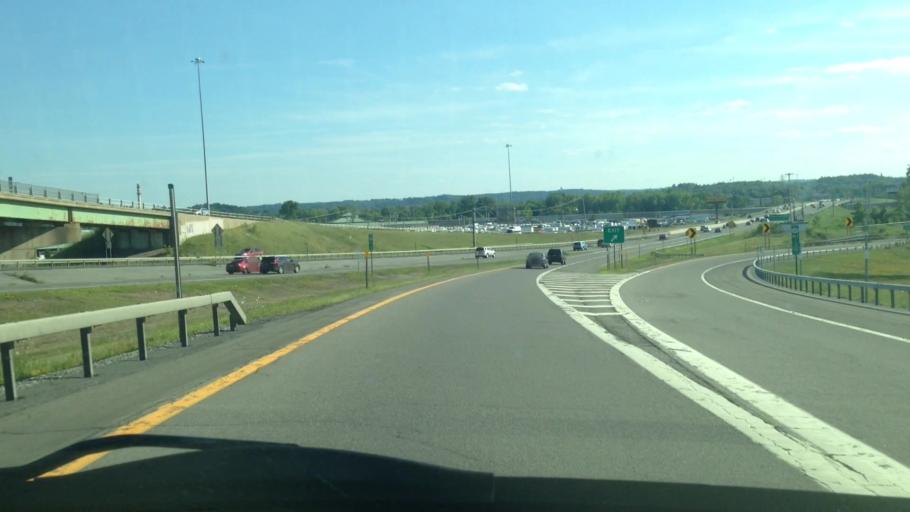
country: US
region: New York
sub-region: Onondaga County
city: Lakeland
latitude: 43.0793
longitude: -76.2263
